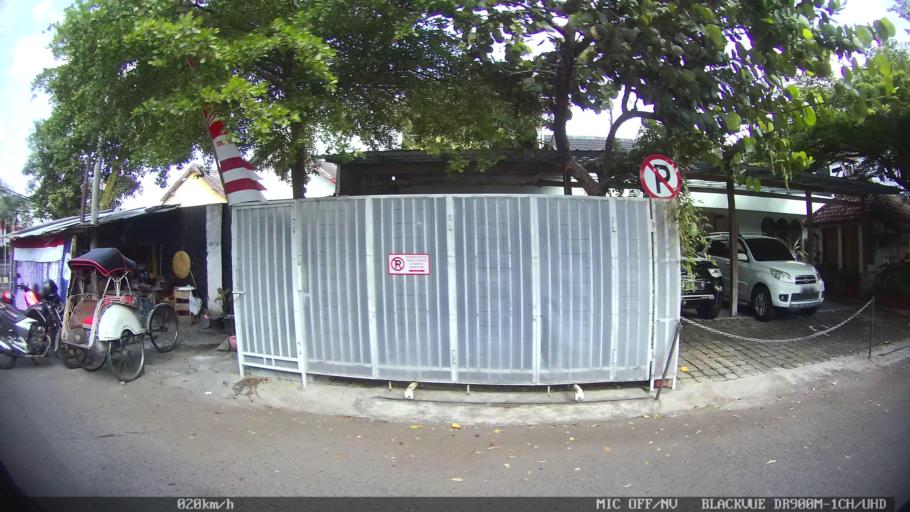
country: ID
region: Daerah Istimewa Yogyakarta
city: Yogyakarta
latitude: -7.7782
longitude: 110.3905
